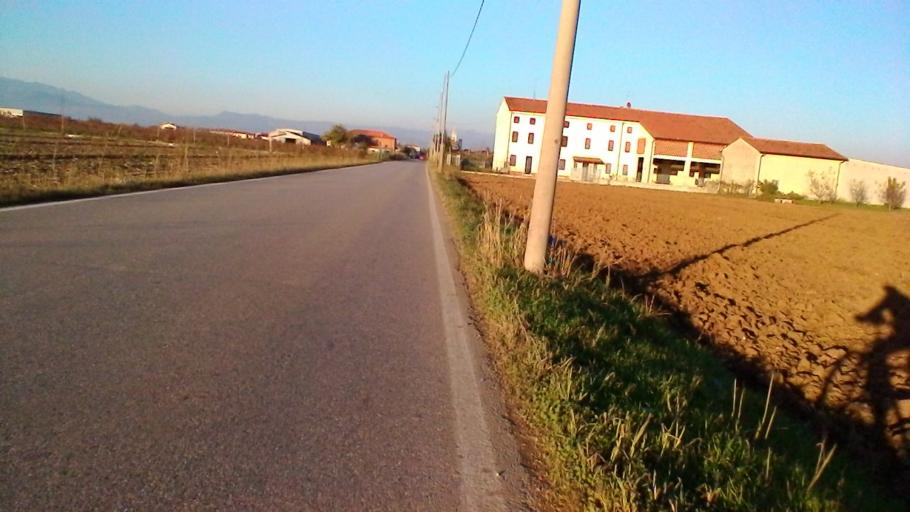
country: IT
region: Veneto
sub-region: Provincia di Verona
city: Alpo
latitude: 45.3658
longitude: 10.9098
